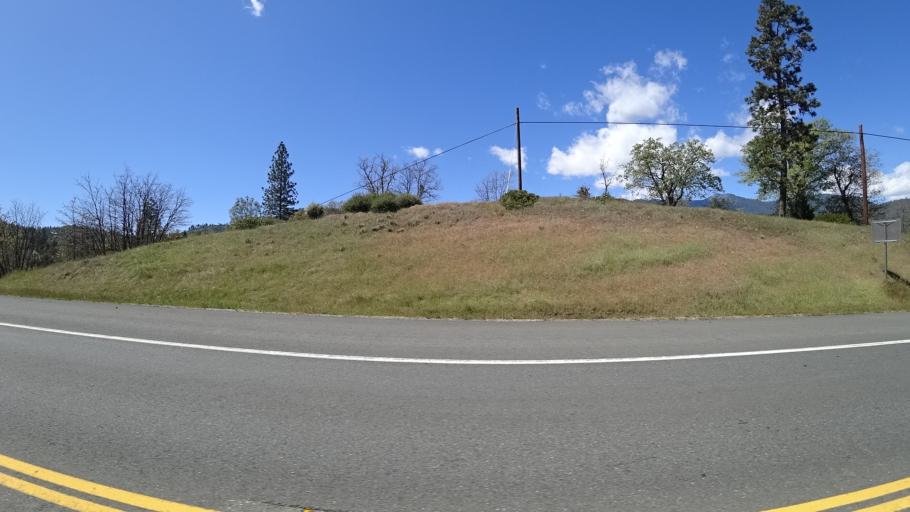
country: US
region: California
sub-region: Trinity County
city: Weaverville
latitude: 40.7358
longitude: -122.9526
